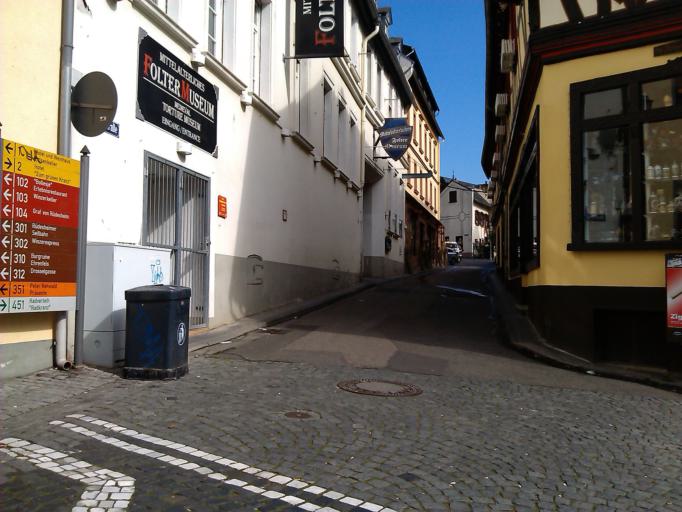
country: DE
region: Hesse
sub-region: Regierungsbezirk Darmstadt
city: Rudesheim am Rhein
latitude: 49.9797
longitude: 7.9222
